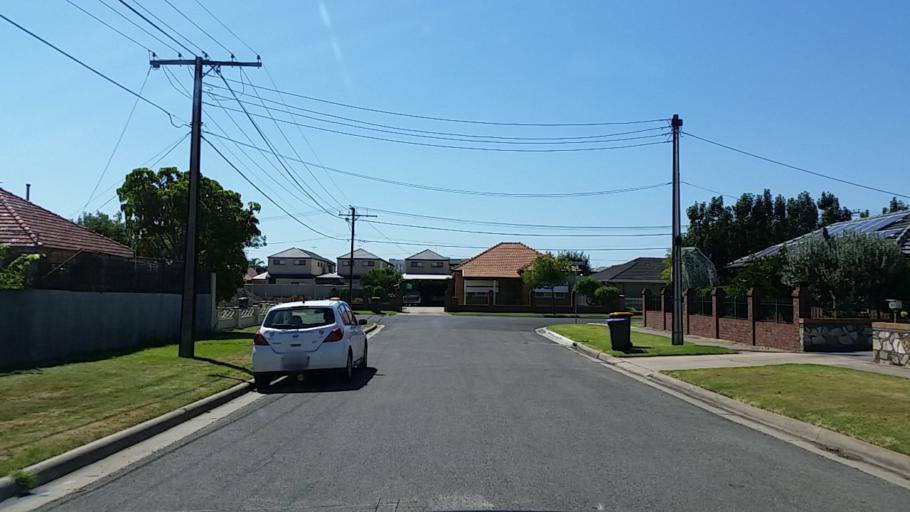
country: AU
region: South Australia
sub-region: Charles Sturt
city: Findon
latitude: -34.9042
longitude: 138.5258
